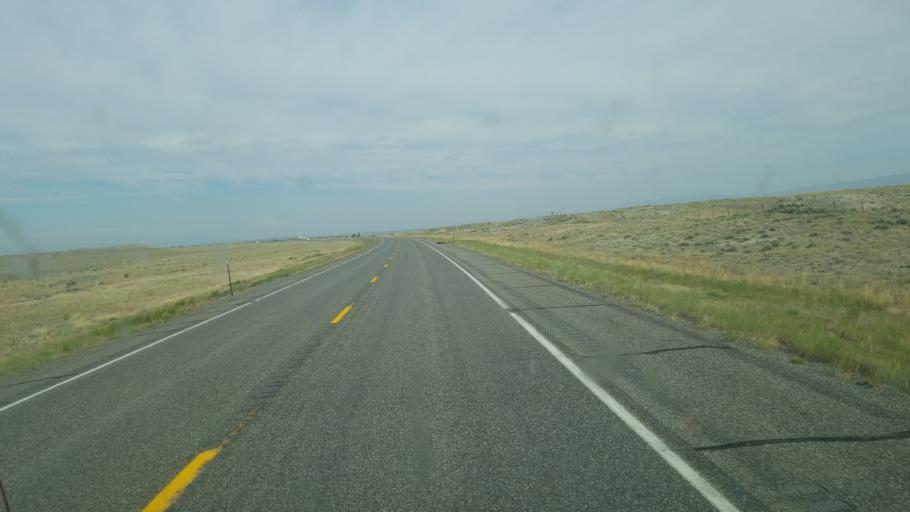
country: US
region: Wyoming
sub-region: Fremont County
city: Riverton
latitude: 43.2353
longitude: -108.0730
